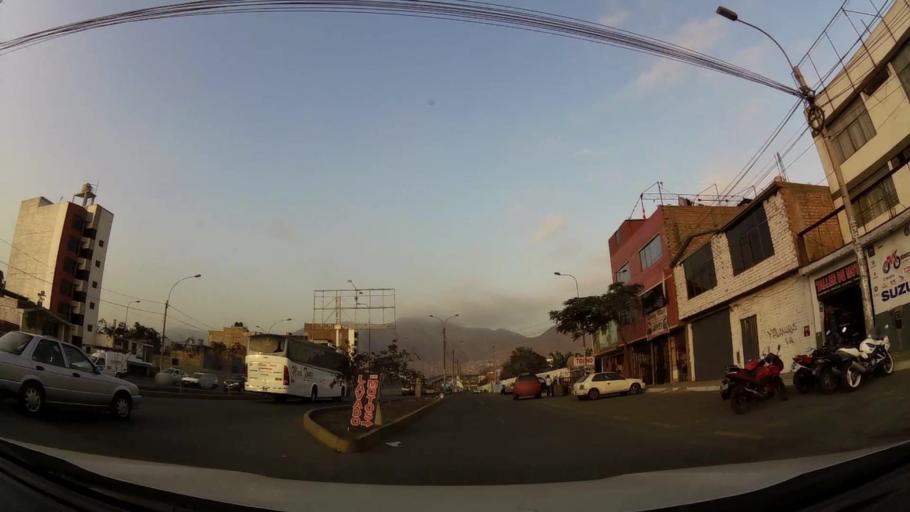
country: PE
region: Lima
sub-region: Lima
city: Independencia
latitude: -12.0053
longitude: -77.0659
